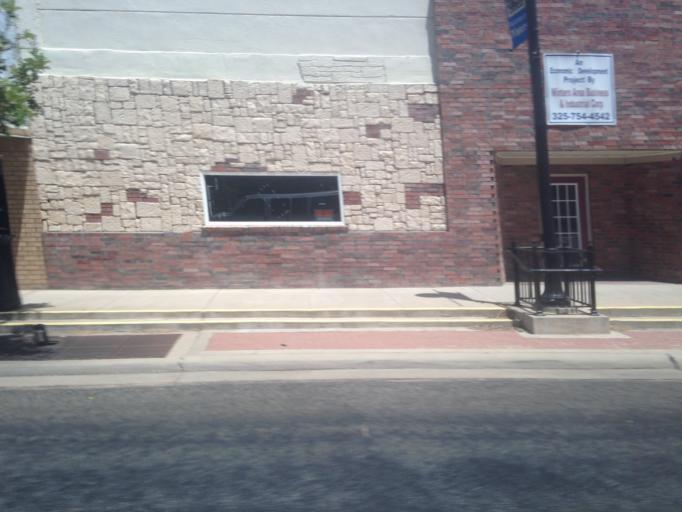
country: US
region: Texas
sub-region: Runnels County
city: Winters
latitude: 31.9569
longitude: -99.9629
